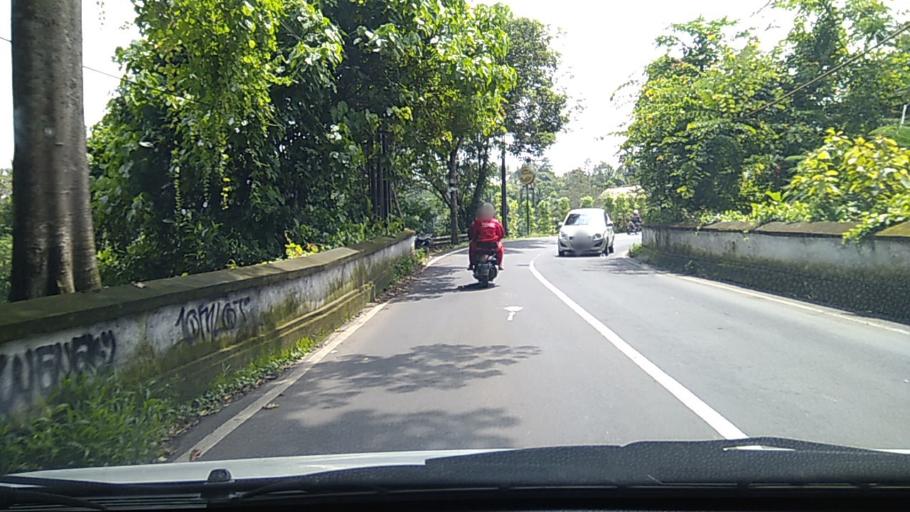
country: ID
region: Bali
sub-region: Kabupaten Gianyar
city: Ubud
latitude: -8.5225
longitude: 115.2840
